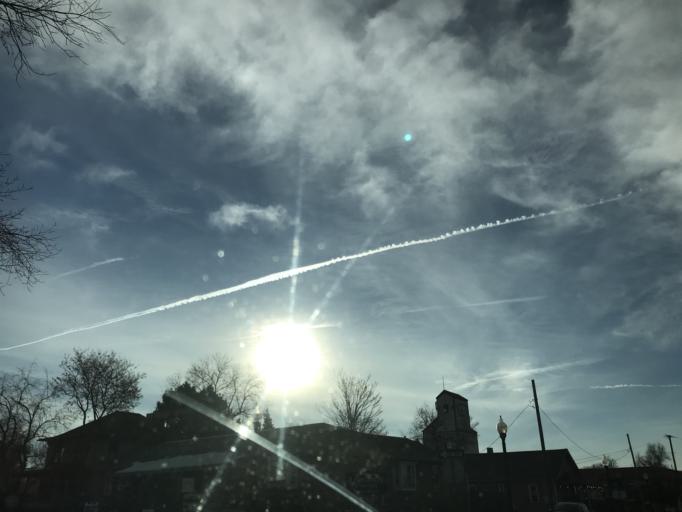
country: US
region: Colorado
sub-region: Arapahoe County
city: Littleton
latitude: 39.6129
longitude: -105.0201
